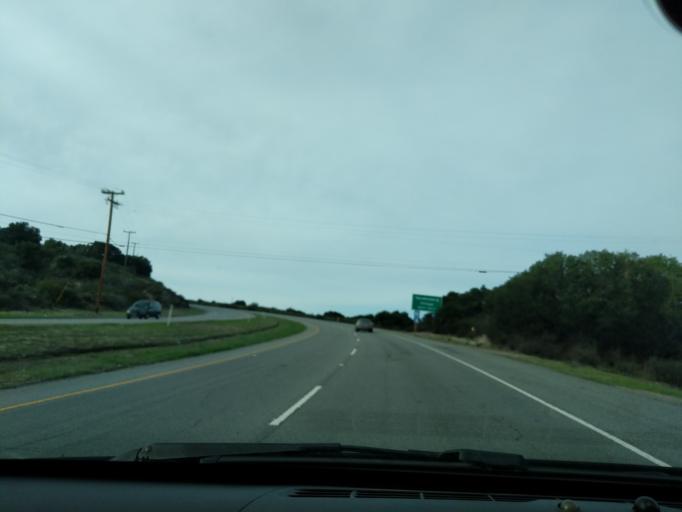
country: US
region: California
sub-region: Santa Barbara County
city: Vandenberg Village
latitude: 34.6937
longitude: -120.4588
